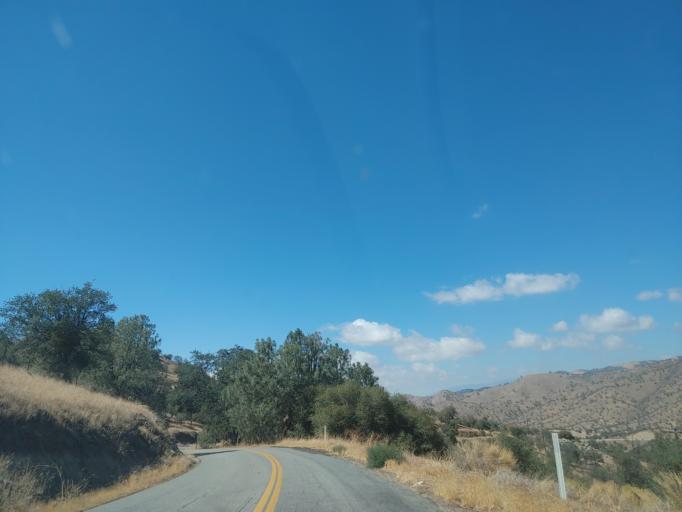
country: US
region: California
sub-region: Kern County
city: Golden Hills
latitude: 35.1825
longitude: -118.5155
